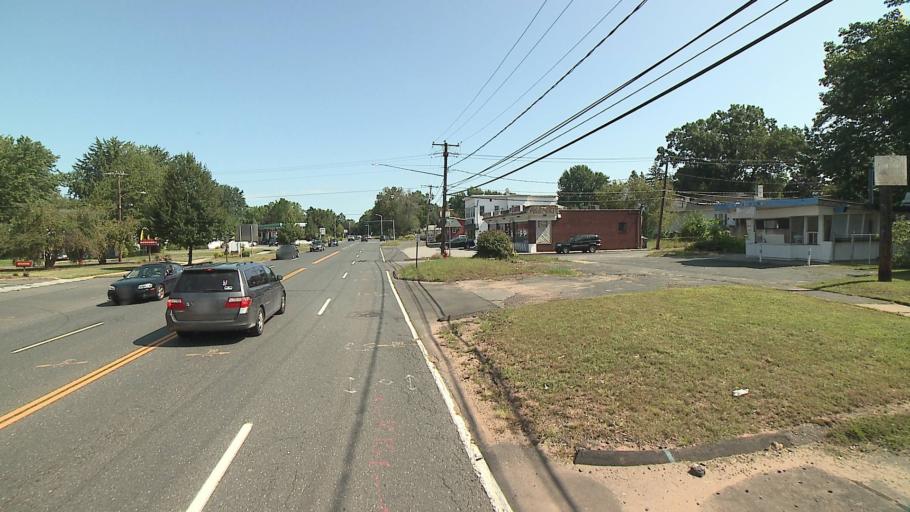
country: US
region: Connecticut
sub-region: Hartford County
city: Sherwood Manor
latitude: 42.0239
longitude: -72.5848
